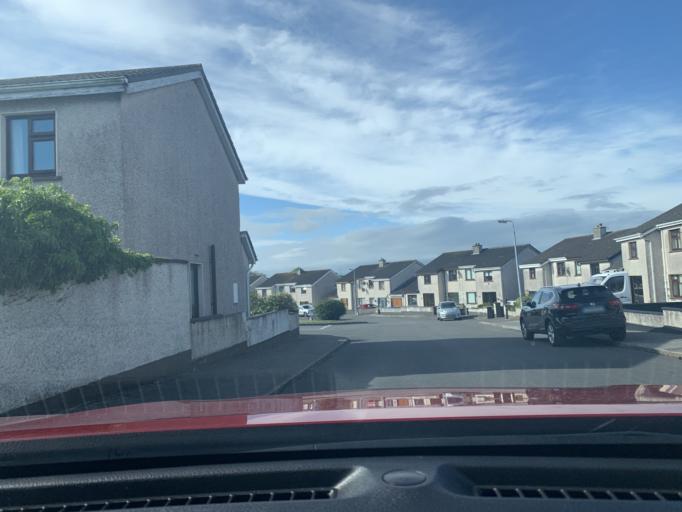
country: IE
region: Connaught
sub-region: Sligo
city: Sligo
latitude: 54.2642
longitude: -8.4996
